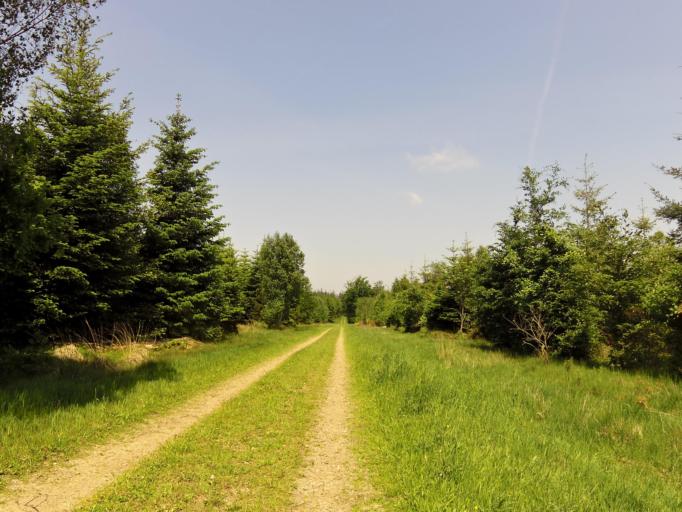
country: DK
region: South Denmark
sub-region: Tonder Kommune
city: Toftlund
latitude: 55.1962
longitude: 8.9606
